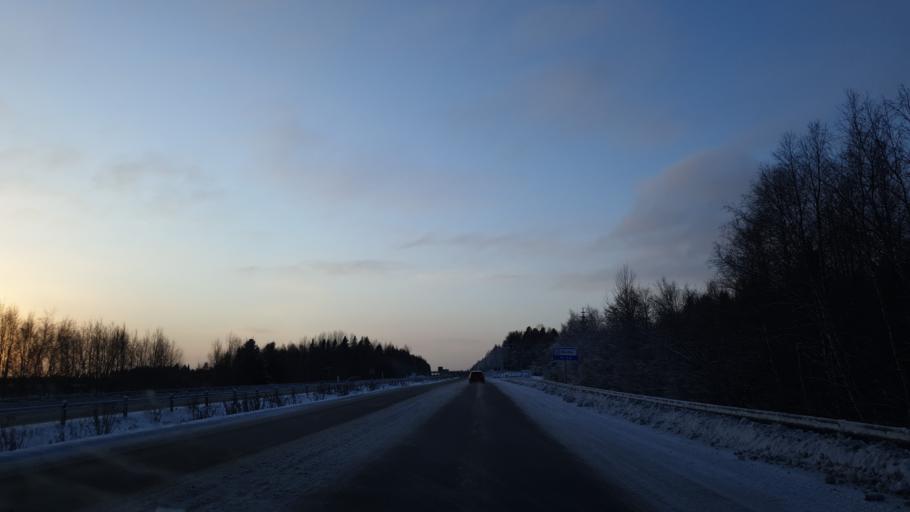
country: SE
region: Vaesterbotten
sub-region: Umea Kommun
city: Roback
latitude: 63.7966
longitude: 20.2241
